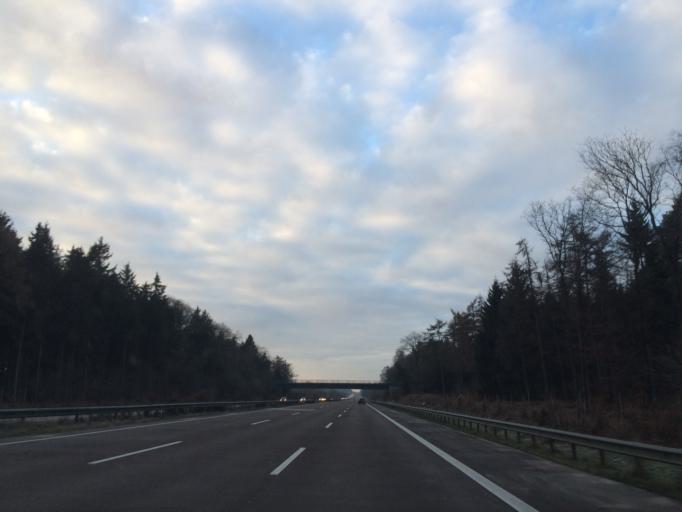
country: DE
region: Schleswig-Holstein
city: Hammoor
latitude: 53.6874
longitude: 10.3180
